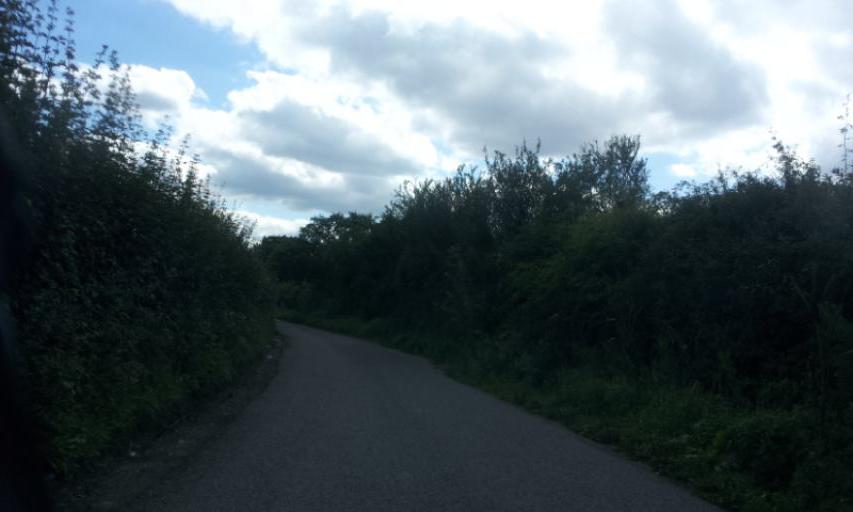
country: GB
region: England
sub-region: Kent
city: Marden
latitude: 51.2114
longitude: 0.5250
